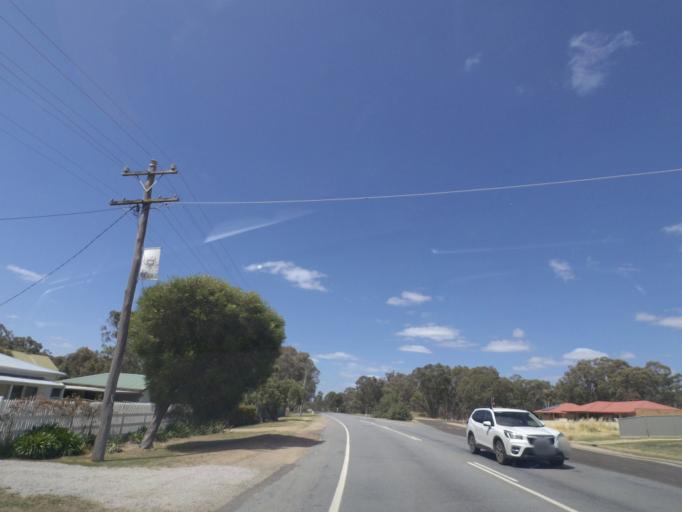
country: AU
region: Victoria
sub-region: Wangaratta
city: Wangaratta
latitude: -36.4633
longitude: 146.2263
